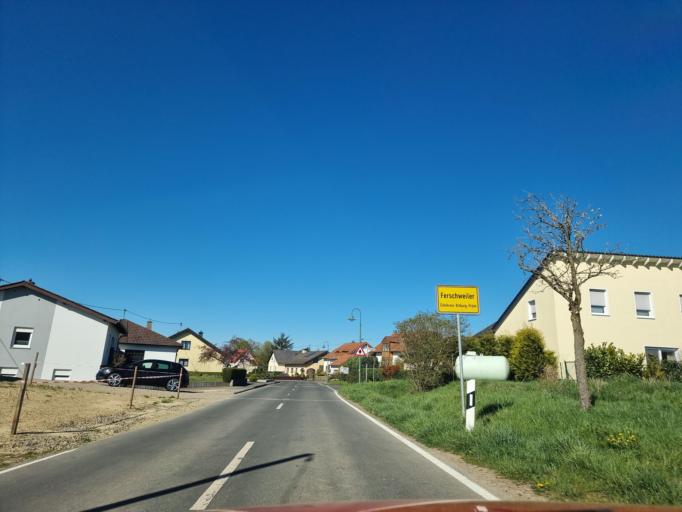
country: DE
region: Rheinland-Pfalz
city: Ernzen
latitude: 49.8620
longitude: 6.4150
